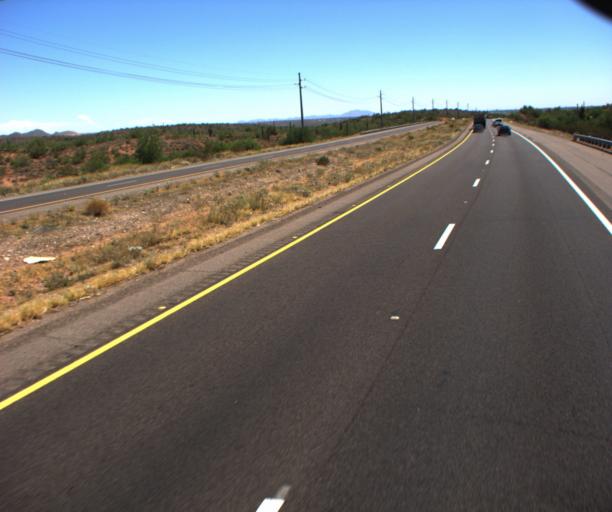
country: US
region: Arizona
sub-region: Maricopa County
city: Fountain Hills
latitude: 33.5477
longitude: -111.7230
